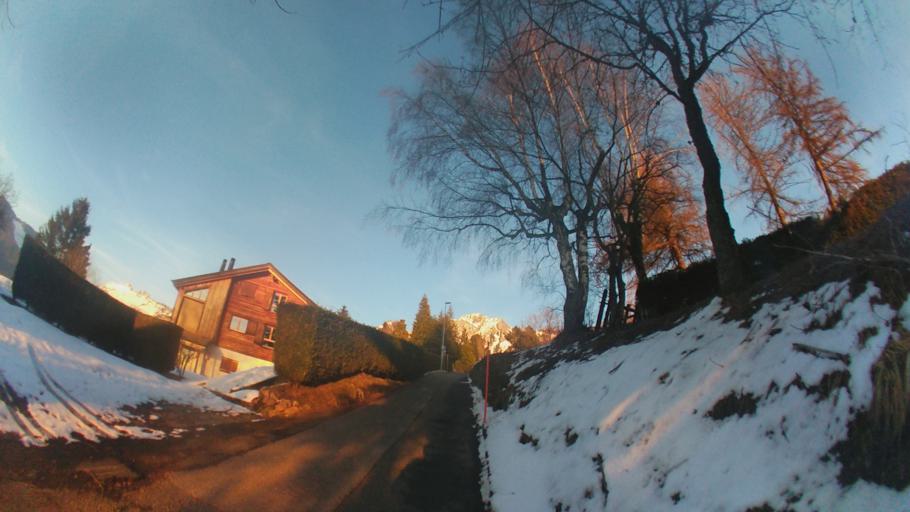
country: CH
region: Vaud
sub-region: Riviera-Pays-d'Enhaut District
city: Caux
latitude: 46.4337
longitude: 6.9444
